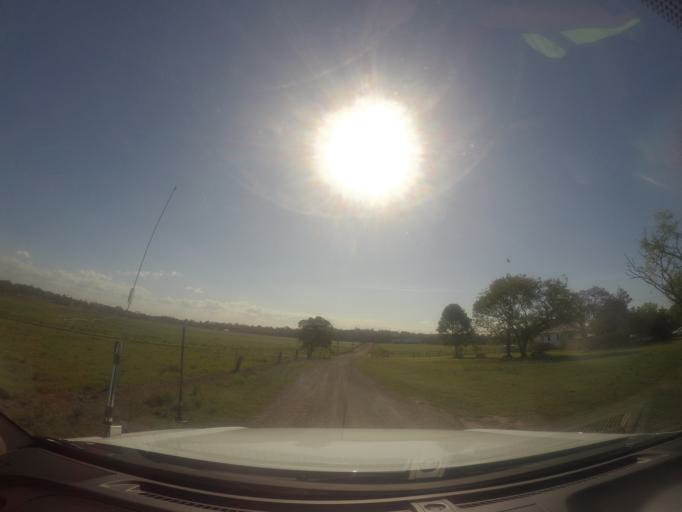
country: AU
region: Queensland
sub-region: Logan
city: Chambers Flat
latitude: -27.7515
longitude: 153.0996
